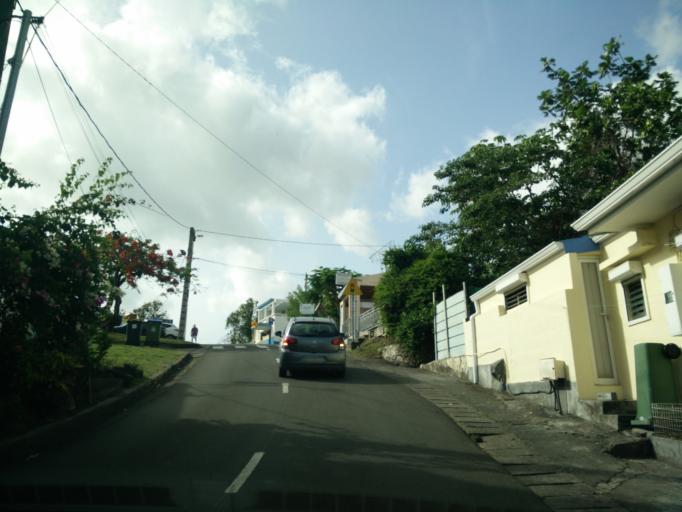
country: MQ
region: Martinique
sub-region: Martinique
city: Saint-Pierre
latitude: 14.8018
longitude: -61.2246
